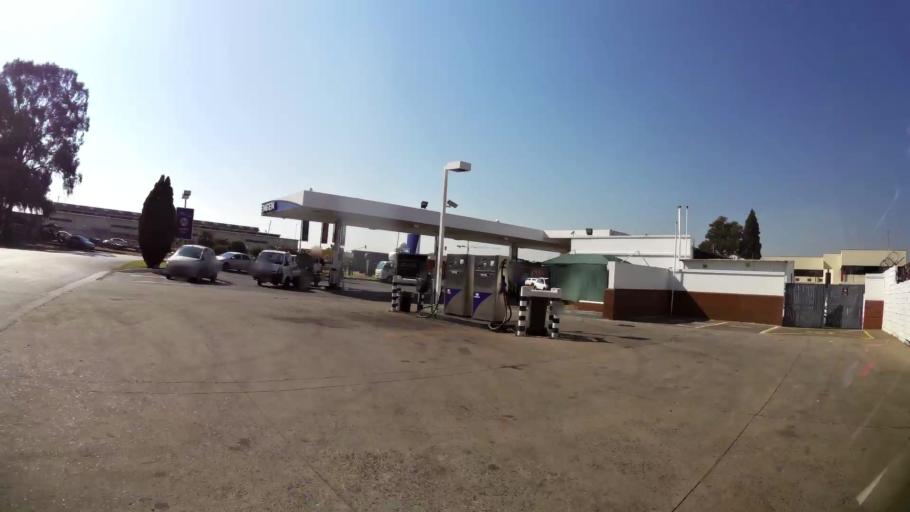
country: ZA
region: Gauteng
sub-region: Ekurhuleni Metropolitan Municipality
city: Boksburg
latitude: -26.1541
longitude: 28.2157
